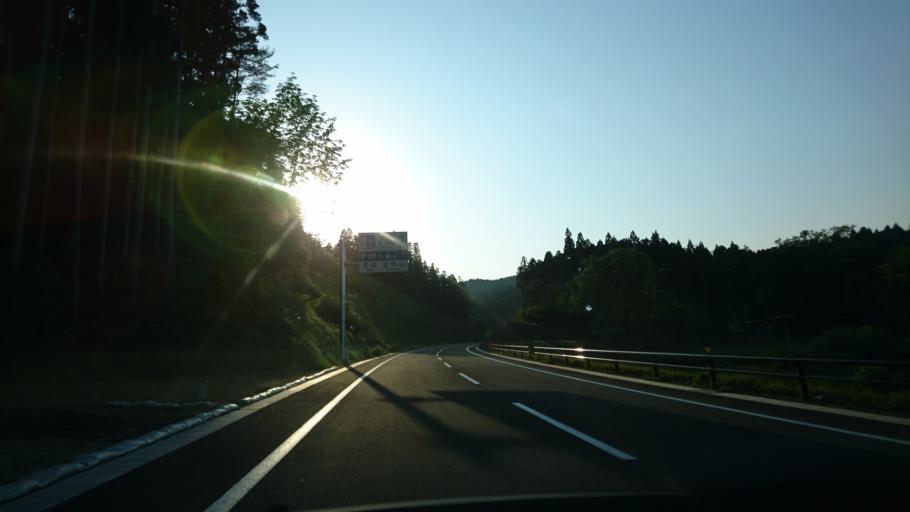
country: JP
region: Iwate
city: Ofunato
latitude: 38.9170
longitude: 141.4602
